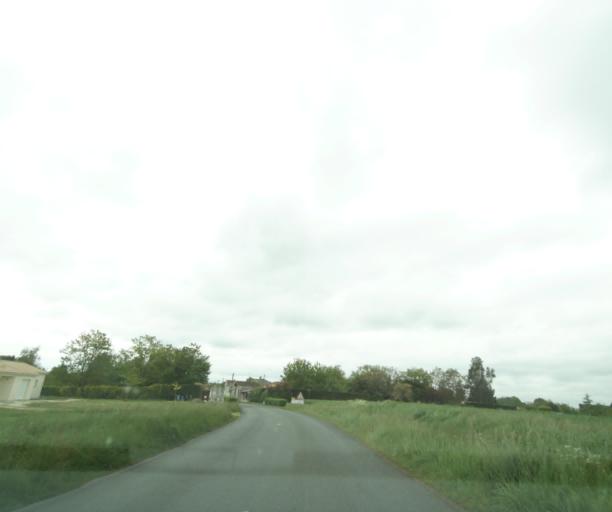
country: FR
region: Poitou-Charentes
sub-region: Departement de la Charente-Maritime
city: Chaniers
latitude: 45.7019
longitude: -0.5511
